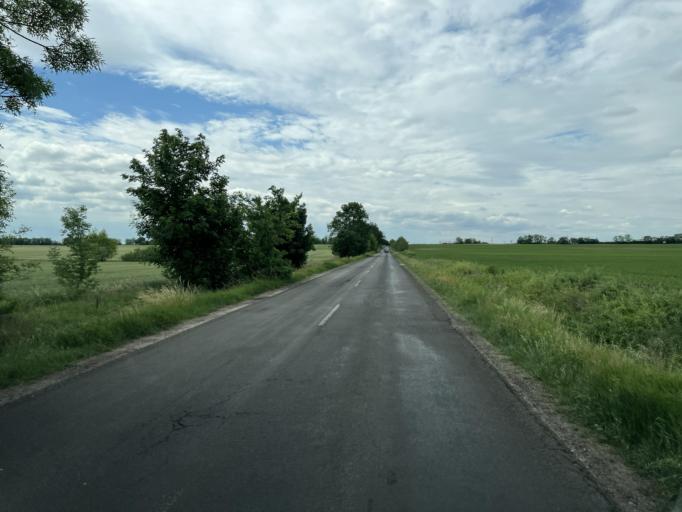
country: HU
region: Pest
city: Szentlorinckata
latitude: 47.4991
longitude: 19.7376
